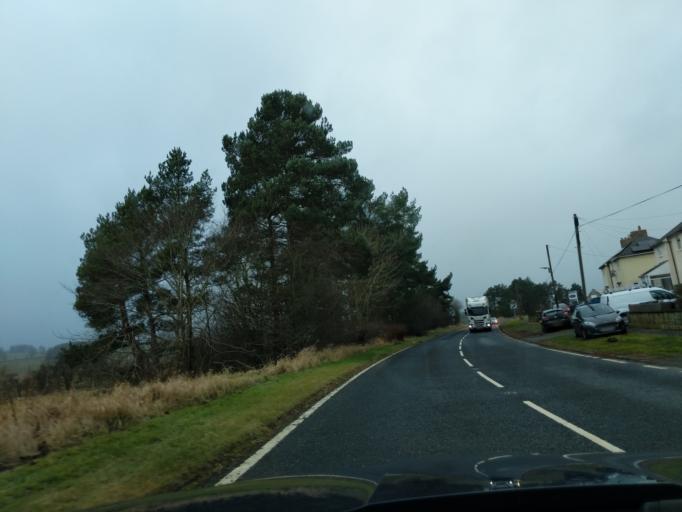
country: GB
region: England
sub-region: Northumberland
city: Otterburn
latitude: 55.2326
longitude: -2.1870
